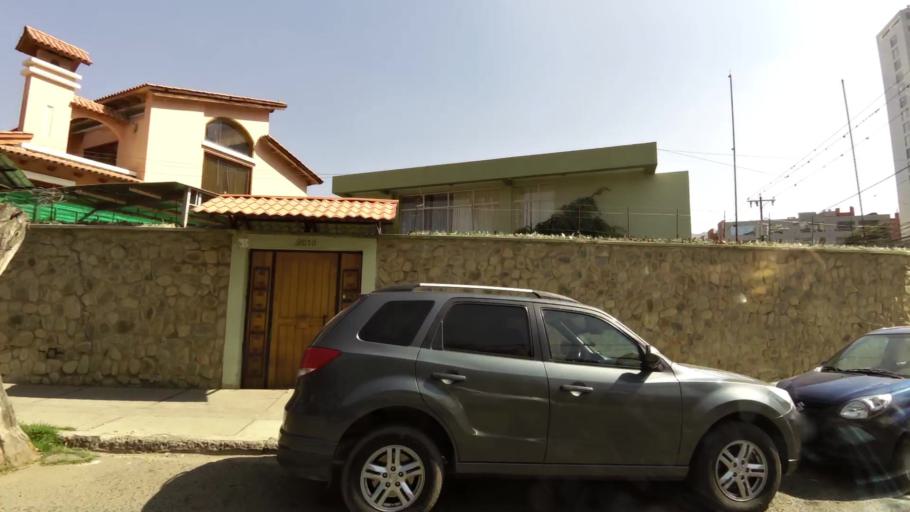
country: BO
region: La Paz
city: La Paz
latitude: -16.5414
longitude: -68.0887
